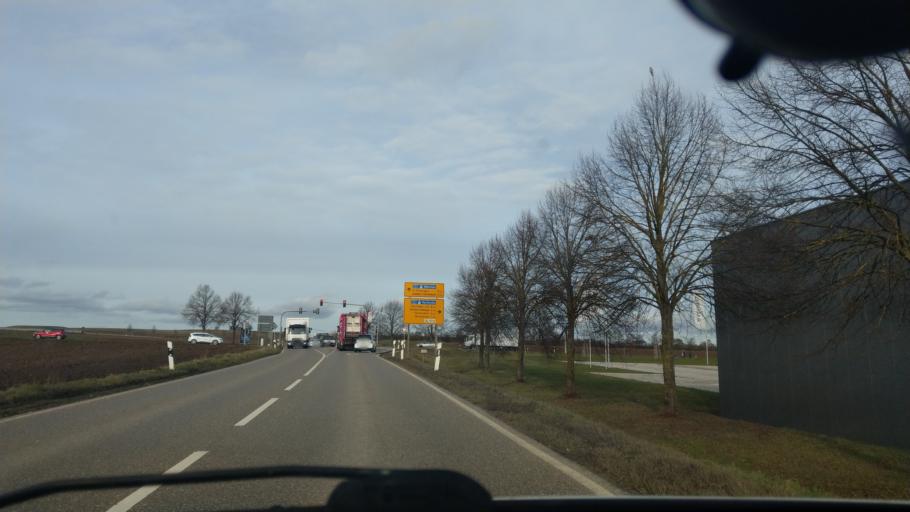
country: DE
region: Baden-Wuerttemberg
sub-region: Regierungsbezirk Stuttgart
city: Neuhausen auf den Fildern
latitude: 48.6909
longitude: 9.2641
